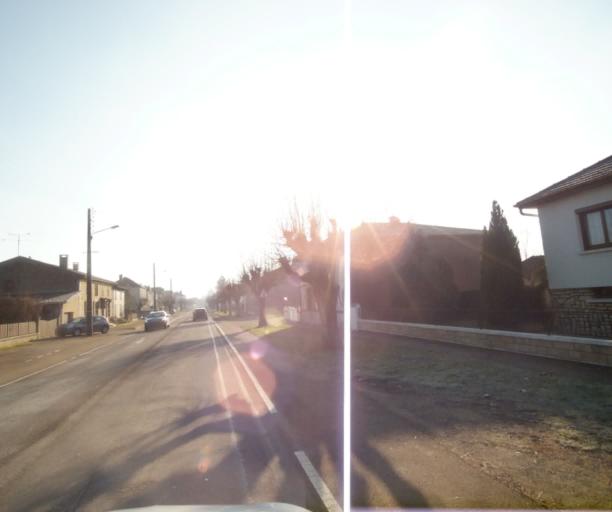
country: FR
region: Champagne-Ardenne
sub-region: Departement de la Haute-Marne
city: Montier-en-Der
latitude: 48.4825
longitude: 4.7644
